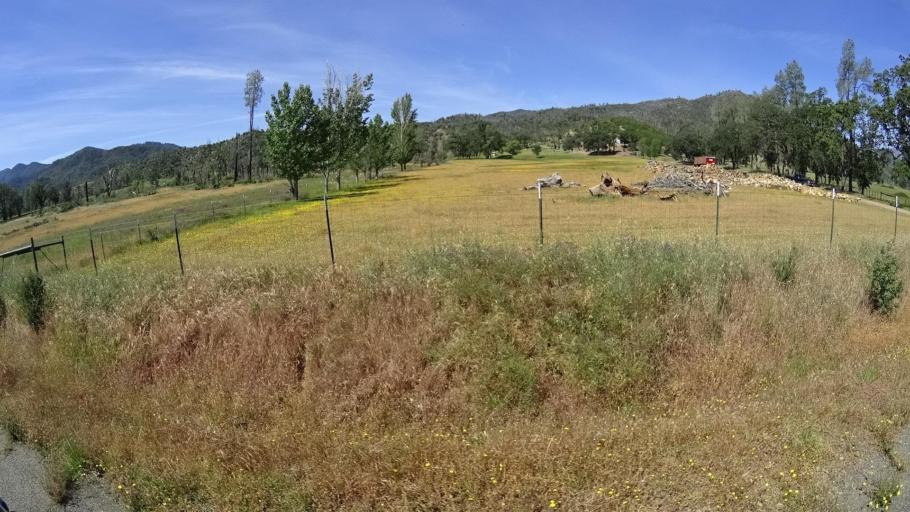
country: US
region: California
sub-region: Lake County
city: Middletown
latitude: 38.7518
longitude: -122.6370
